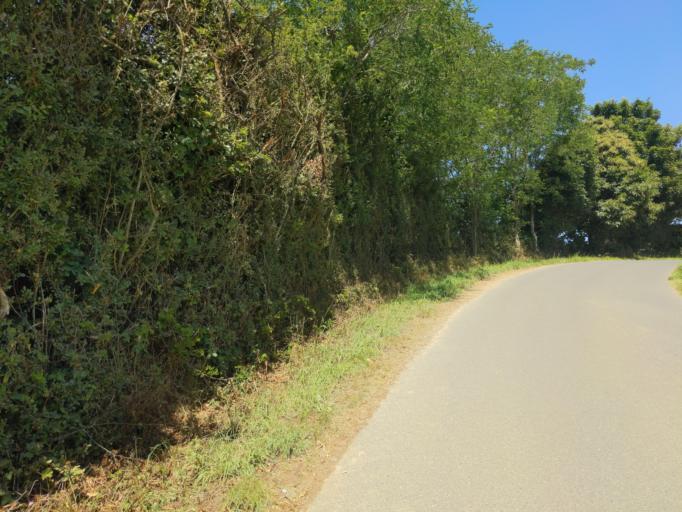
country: FR
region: Brittany
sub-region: Departement des Cotes-d'Armor
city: Plouguiel
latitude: 48.8026
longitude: -3.2271
